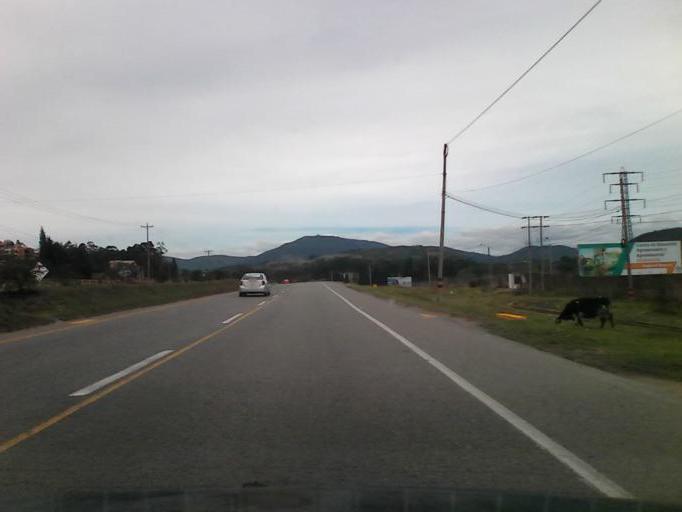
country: CO
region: Boyaca
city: Duitama
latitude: 5.7901
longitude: -73.0538
